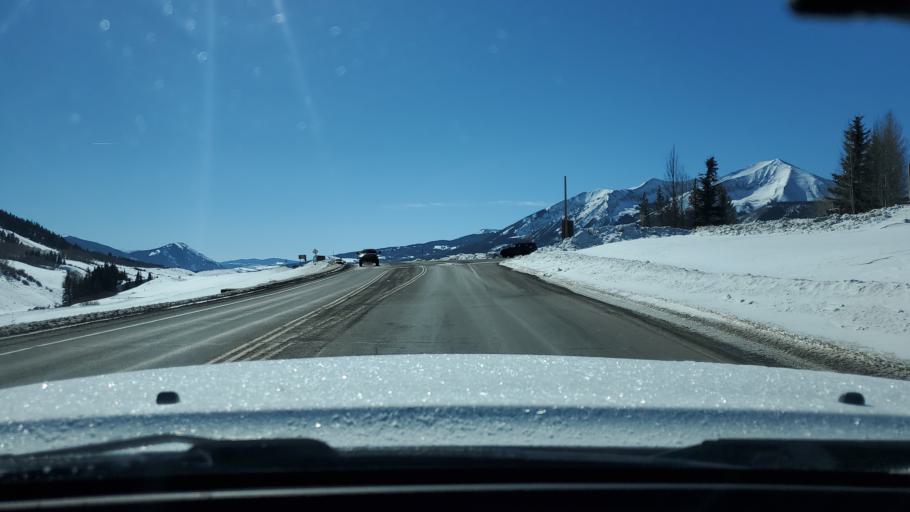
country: US
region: Colorado
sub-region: Gunnison County
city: Crested Butte
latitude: 38.8907
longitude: -106.9727
